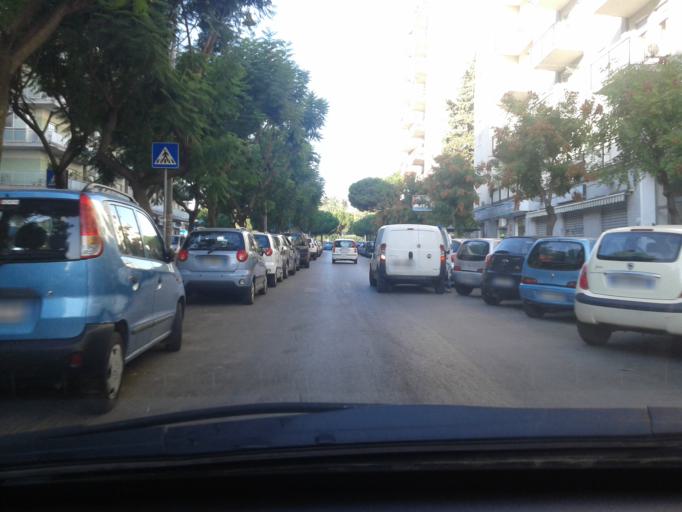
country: IT
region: Sicily
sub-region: Palermo
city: Palermo
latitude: 38.1008
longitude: 13.3332
